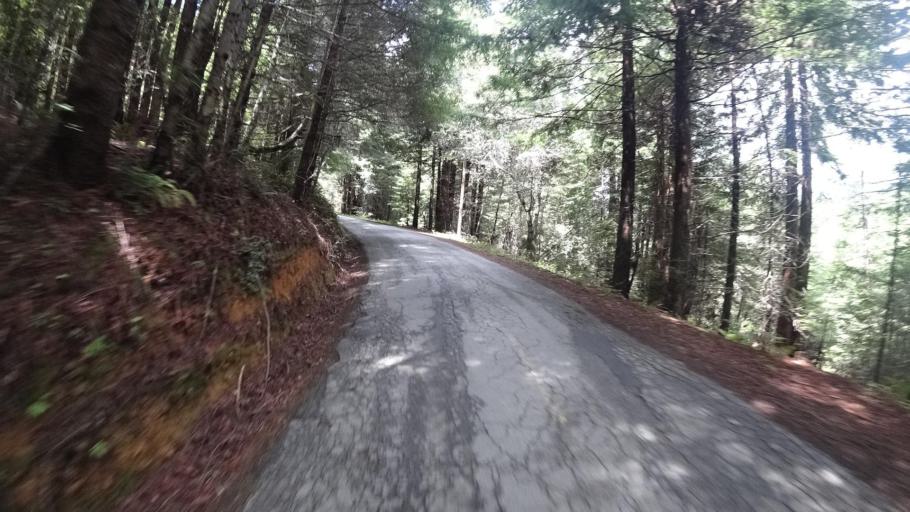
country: US
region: California
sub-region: Humboldt County
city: Blue Lake
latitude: 40.8025
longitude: -123.8800
